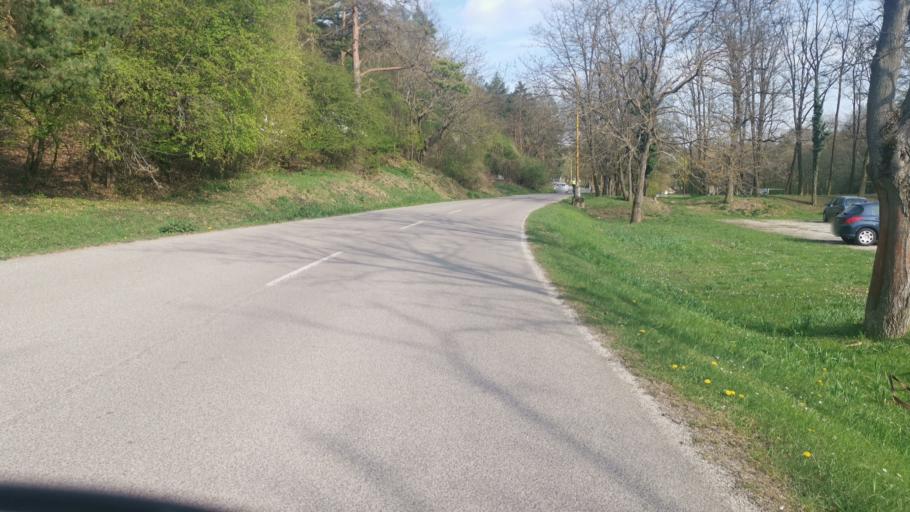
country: CZ
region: South Moravian
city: Sudomerice
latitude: 48.8277
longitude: 17.2950
